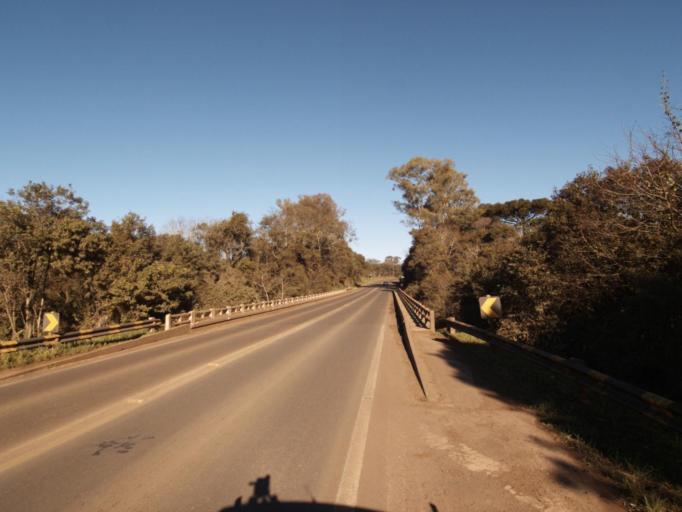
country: BR
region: Rio Grande do Sul
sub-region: Frederico Westphalen
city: Frederico Westphalen
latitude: -26.8900
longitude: -53.1809
